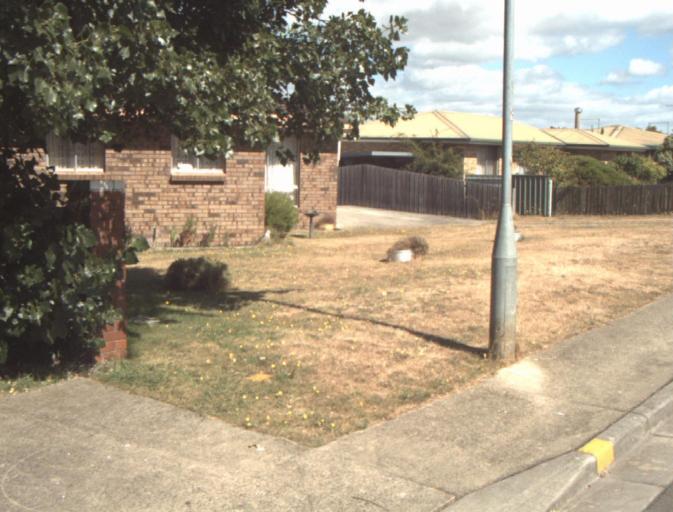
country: AU
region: Tasmania
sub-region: Launceston
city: Newstead
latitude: -41.4217
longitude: 147.1814
